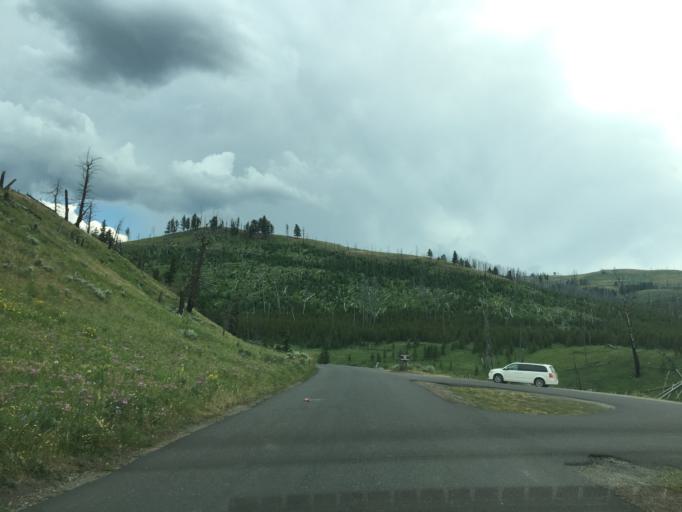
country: US
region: Montana
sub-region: Gallatin County
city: West Yellowstone
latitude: 44.9200
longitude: -110.4428
